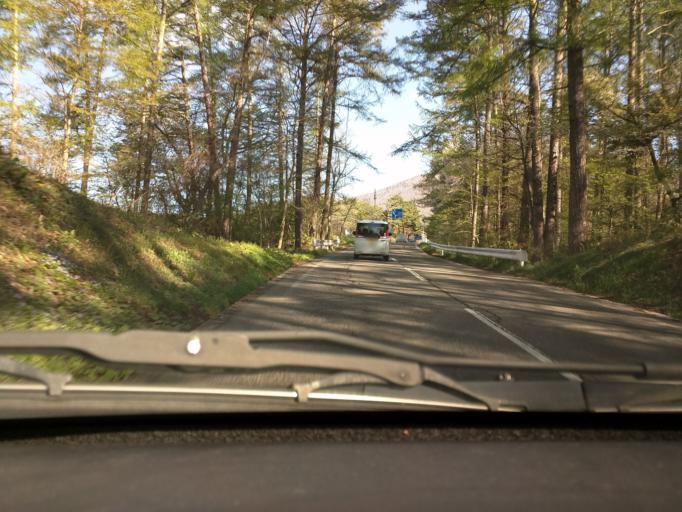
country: JP
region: Nagano
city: Nagano-shi
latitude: 36.7048
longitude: 138.1462
